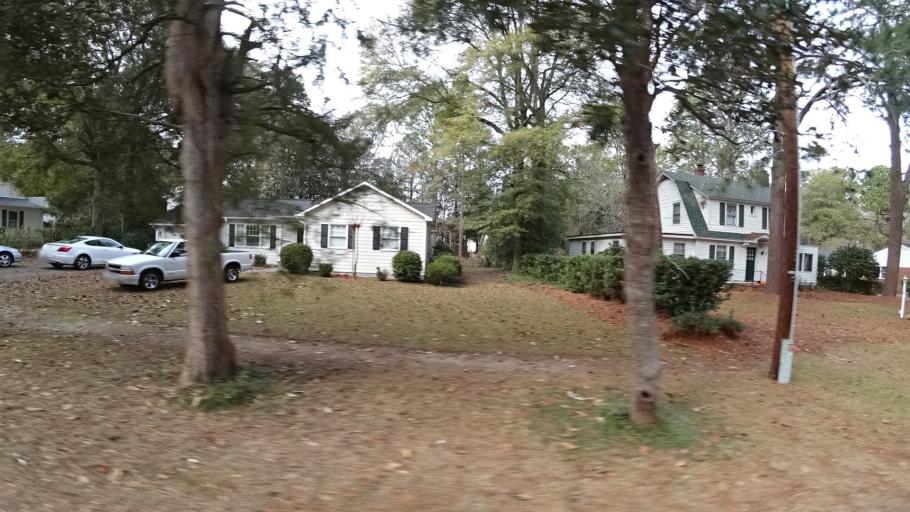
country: US
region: North Carolina
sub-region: Moore County
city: Pinehurst
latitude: 35.1997
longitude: -79.4611
